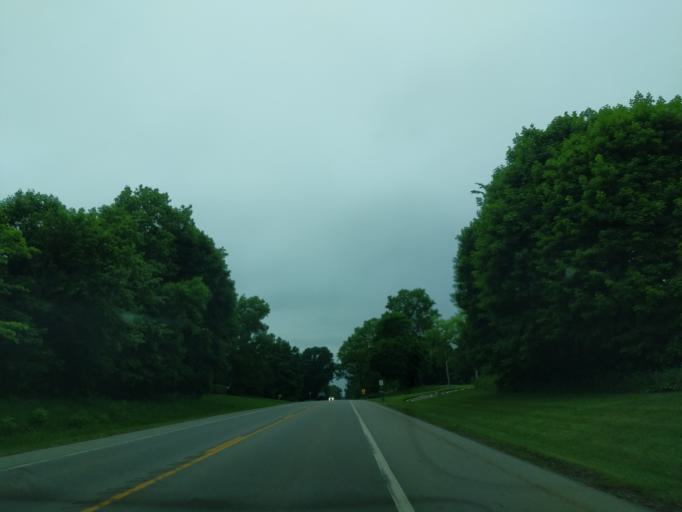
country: US
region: Michigan
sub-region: Branch County
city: Quincy
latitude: 41.9488
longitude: -84.8367
